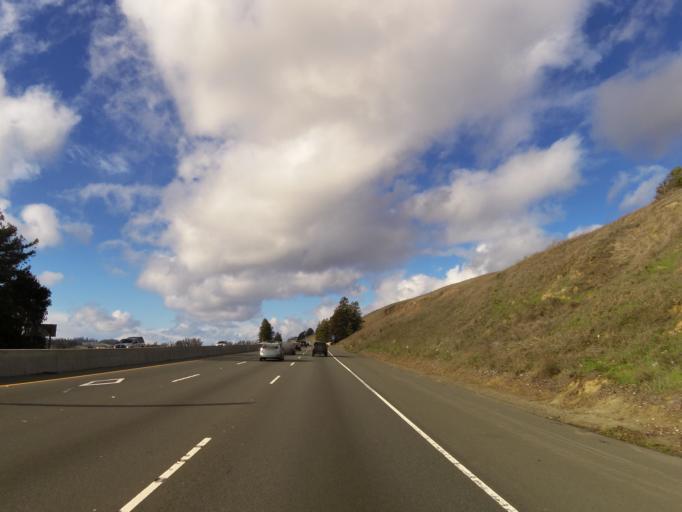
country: US
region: California
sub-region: Sonoma County
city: Penngrove
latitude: 38.2865
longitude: -122.6886
